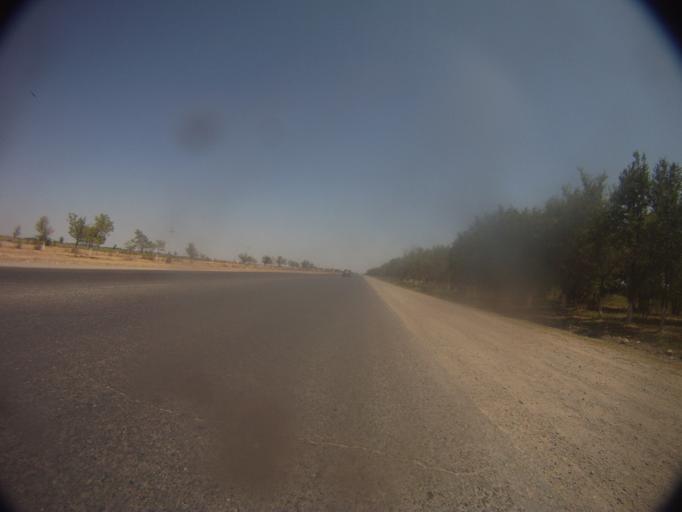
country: KZ
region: Zhambyl
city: Taraz
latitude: 42.8349
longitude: 71.2010
